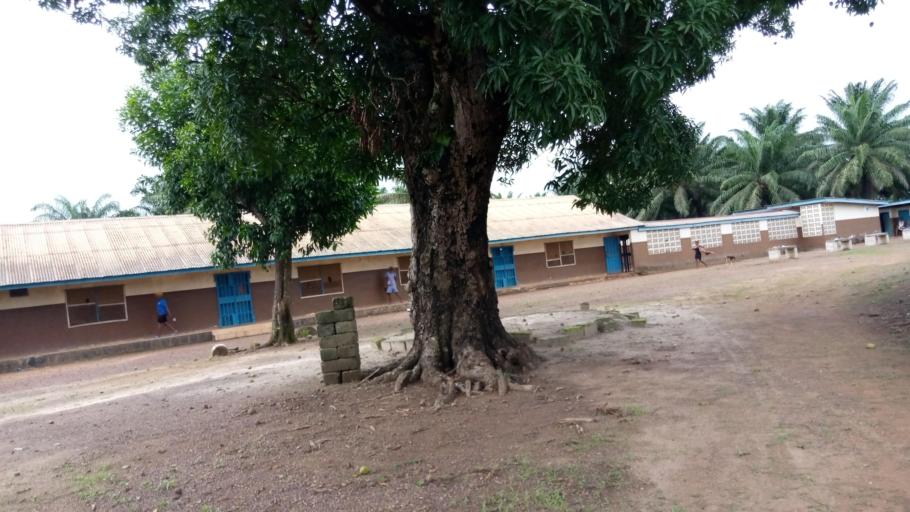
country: SL
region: Southern Province
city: Moyamba
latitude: 8.1518
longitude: -12.4305
